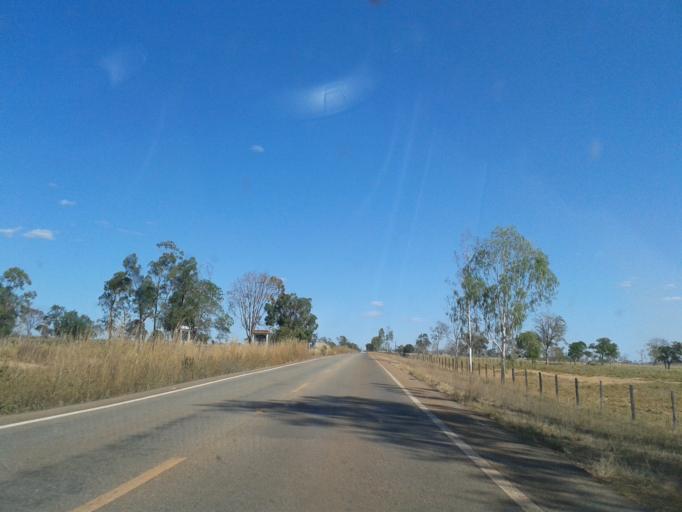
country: BR
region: Goias
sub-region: Crixas
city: Crixas
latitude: -14.2275
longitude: -50.3936
